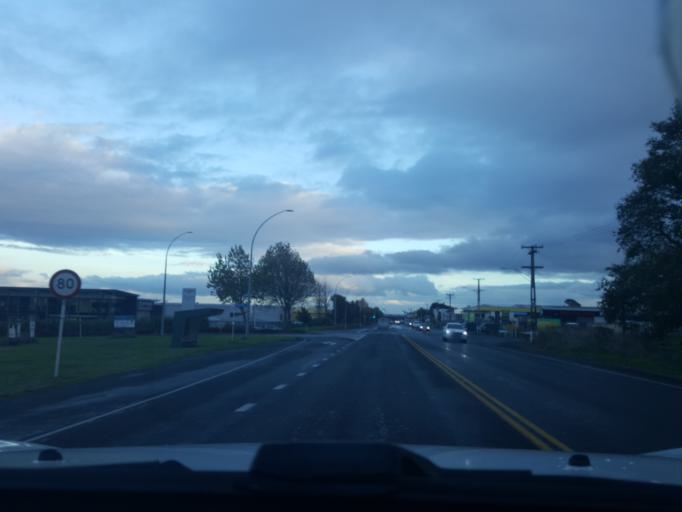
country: NZ
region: Waikato
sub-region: Waikato District
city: Ngaruawahia
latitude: -37.7264
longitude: 175.2185
